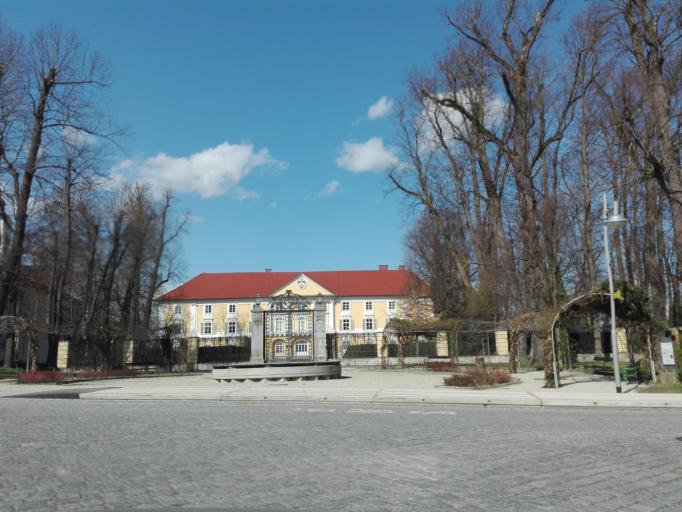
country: AT
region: Upper Austria
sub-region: Politischer Bezirk Urfahr-Umgebung
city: Feldkirchen an der Donau
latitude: 48.3100
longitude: 14.0235
